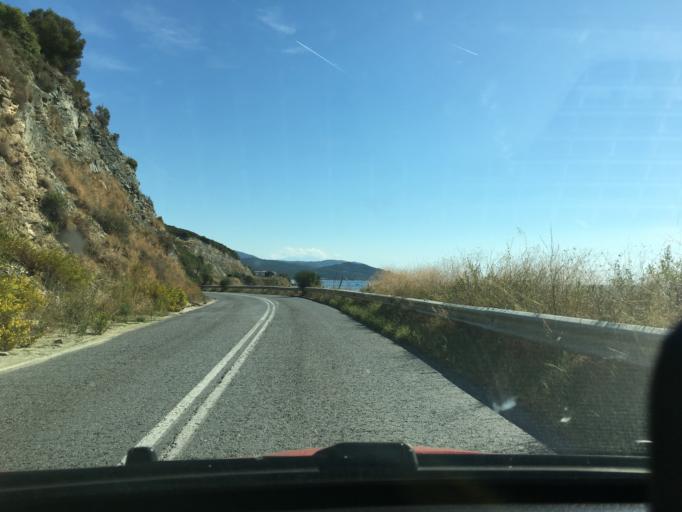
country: GR
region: Central Macedonia
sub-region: Nomos Chalkidikis
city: Nea Roda
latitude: 40.3575
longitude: 23.9406
